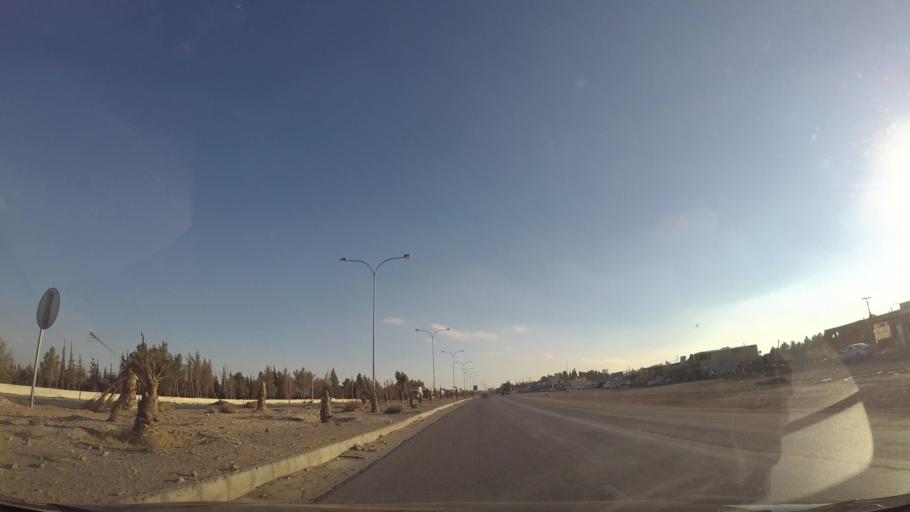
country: JO
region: Tafielah
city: Busayra
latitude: 30.6011
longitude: 35.8052
